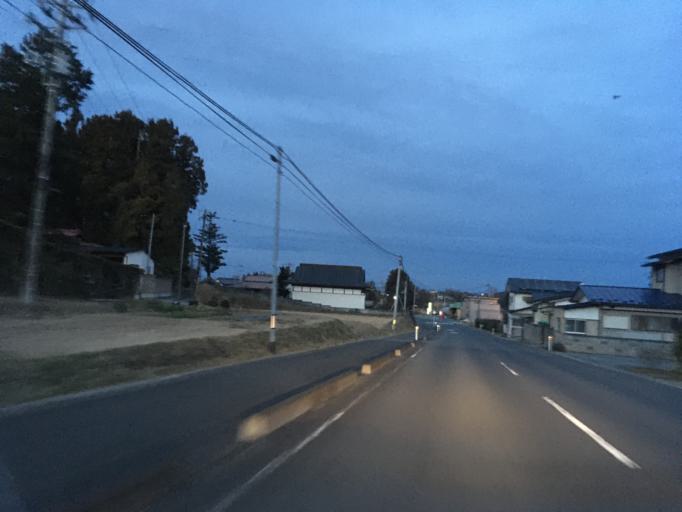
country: JP
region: Miyagi
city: Wakuya
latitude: 38.7054
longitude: 141.1180
